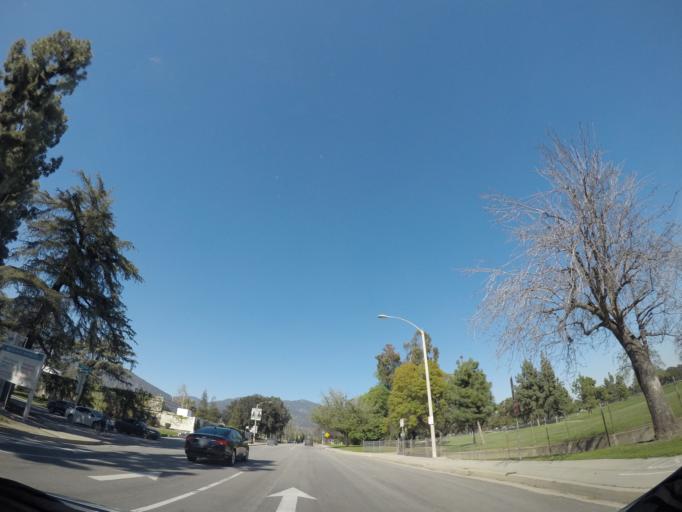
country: US
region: California
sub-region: Los Angeles County
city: Arcadia
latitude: 34.1353
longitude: -118.0396
